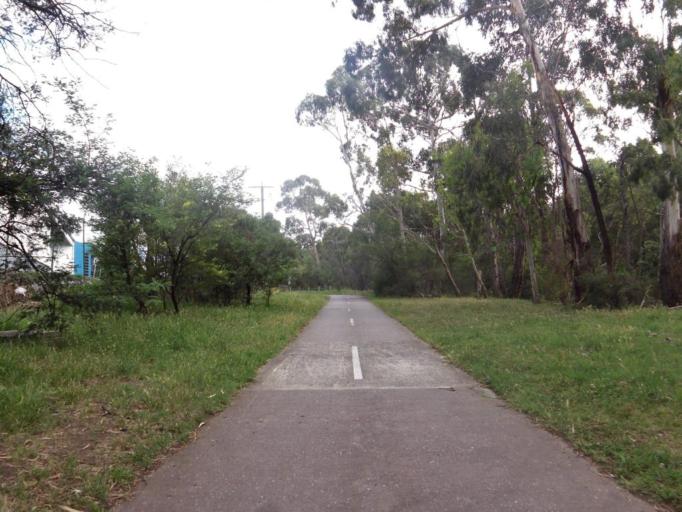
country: AU
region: Victoria
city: Alphington
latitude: -37.7677
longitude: 145.0314
